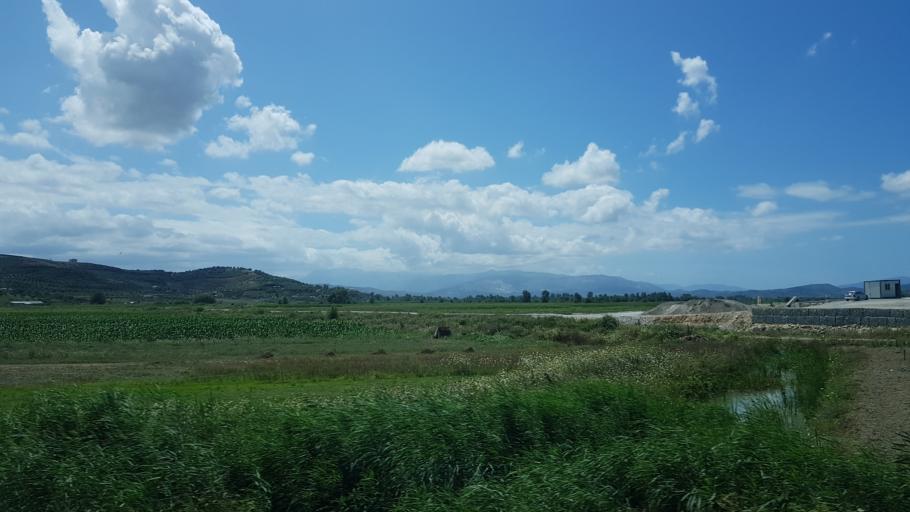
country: AL
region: Fier
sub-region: Rrethi i Fierit
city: Cakran
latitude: 40.5941
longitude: 19.5778
